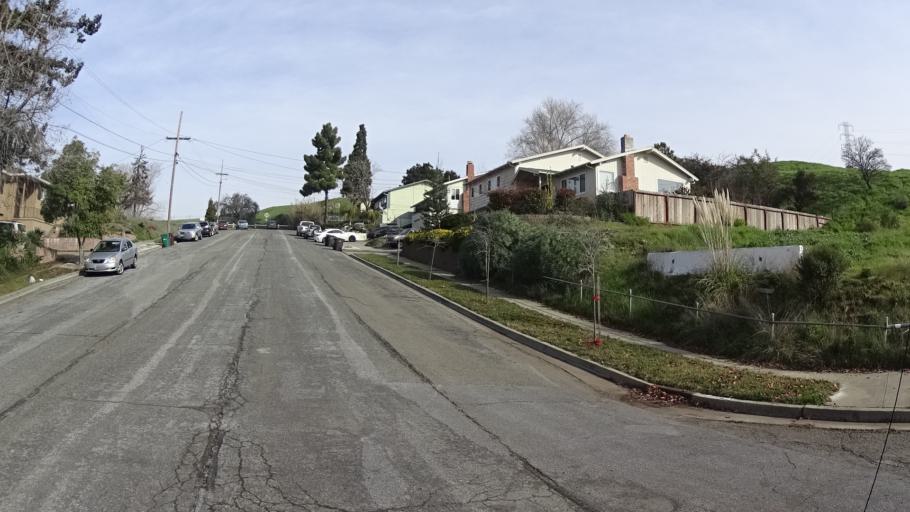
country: US
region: California
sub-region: Alameda County
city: Hayward
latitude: 37.6620
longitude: -122.0694
